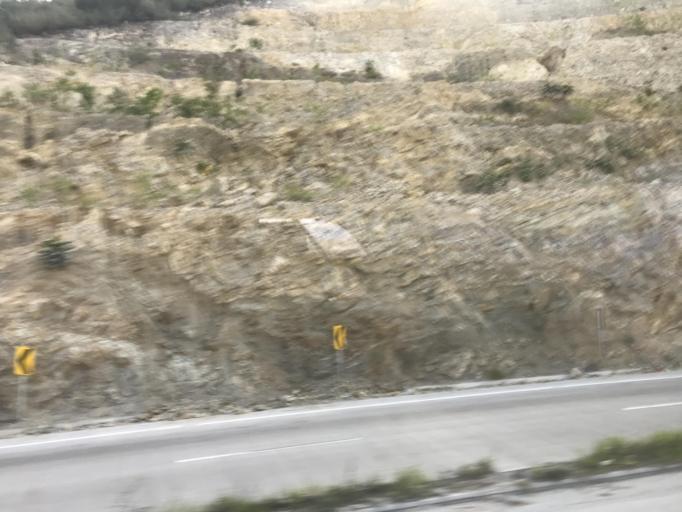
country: GT
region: El Progreso
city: Guastatoya
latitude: 14.8467
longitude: -90.1133
